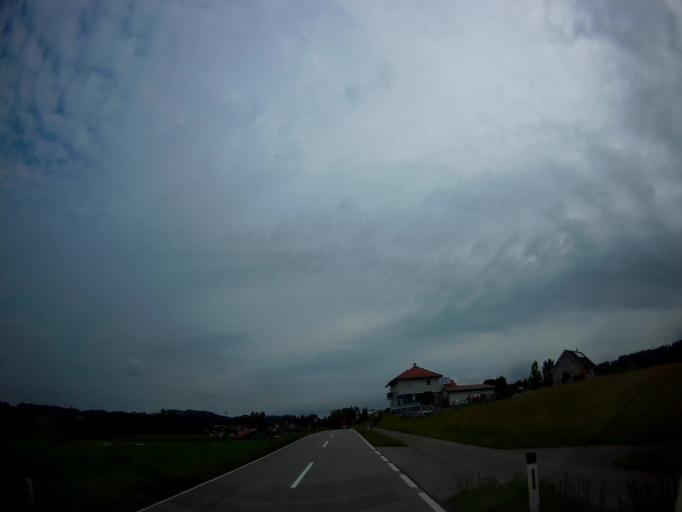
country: AT
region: Salzburg
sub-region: Politischer Bezirk Salzburg-Umgebung
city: Mattsee
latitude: 48.0044
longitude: 13.1240
